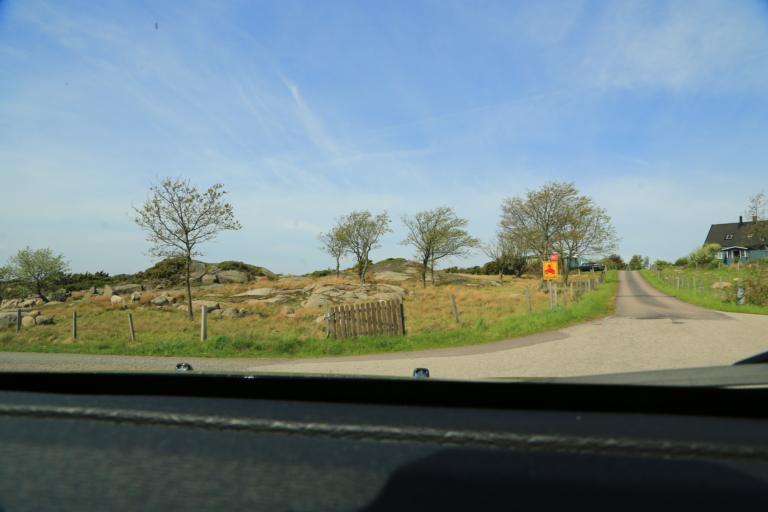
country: SE
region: Halland
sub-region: Varbergs Kommun
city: Varberg
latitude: 57.1413
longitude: 12.2189
